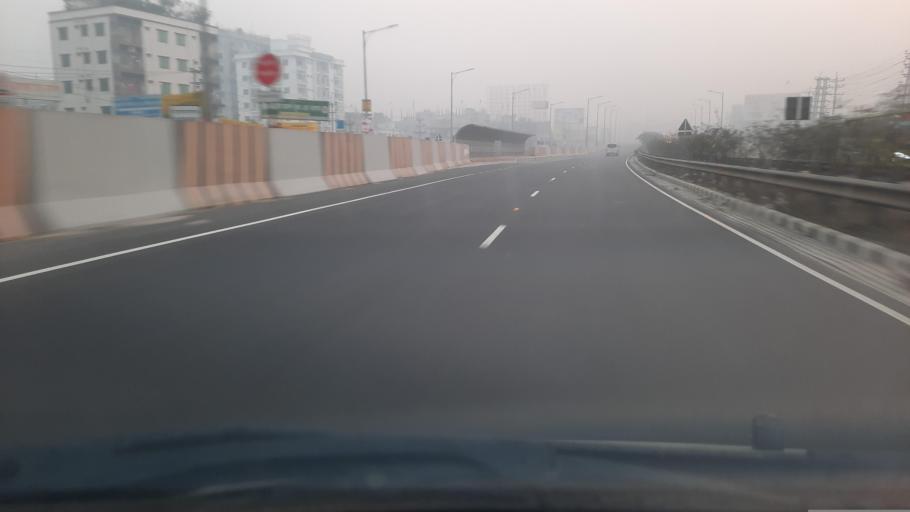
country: BD
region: Dhaka
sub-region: Dhaka
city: Dhaka
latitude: 23.6827
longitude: 90.4163
